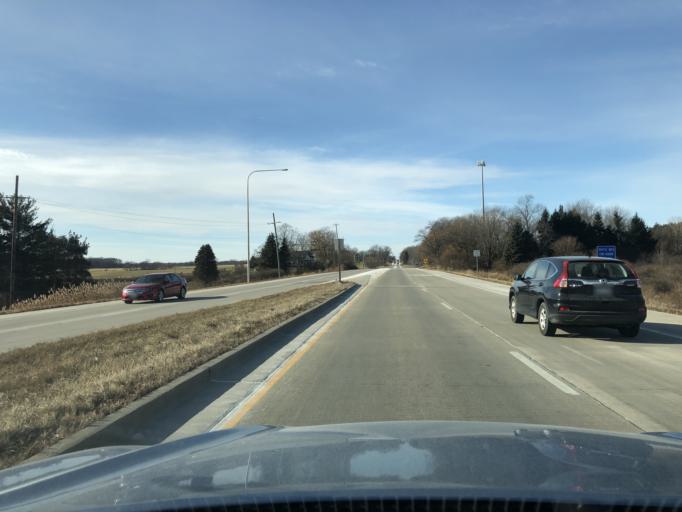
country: US
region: Illinois
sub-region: Lake County
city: Wadsworth
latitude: 42.4657
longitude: -87.9676
